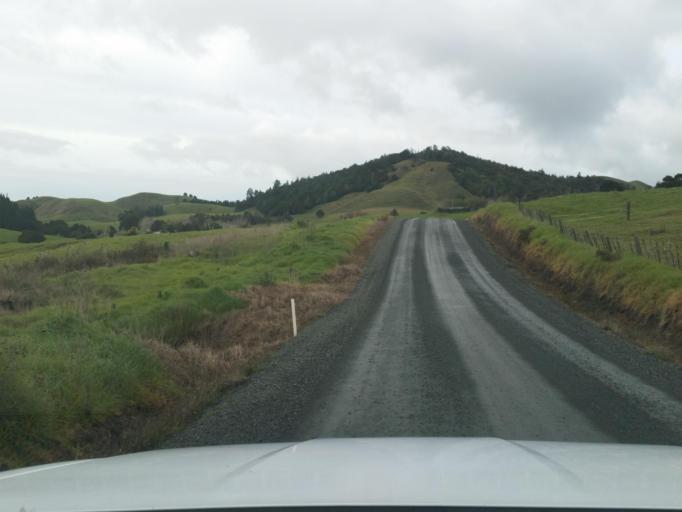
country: NZ
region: Northland
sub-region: Kaipara District
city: Dargaville
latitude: -35.8219
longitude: 173.8157
